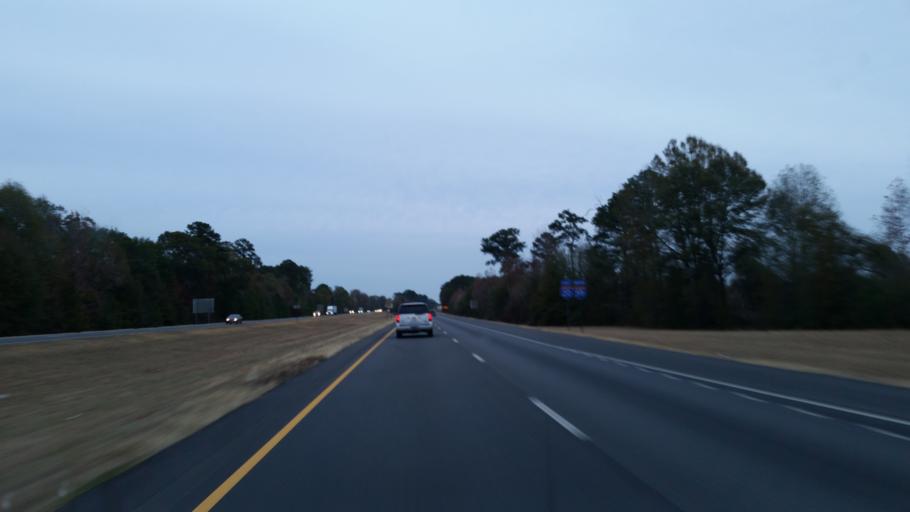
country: US
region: Alabama
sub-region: Greene County
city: Eutaw
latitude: 32.7997
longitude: -88.0268
